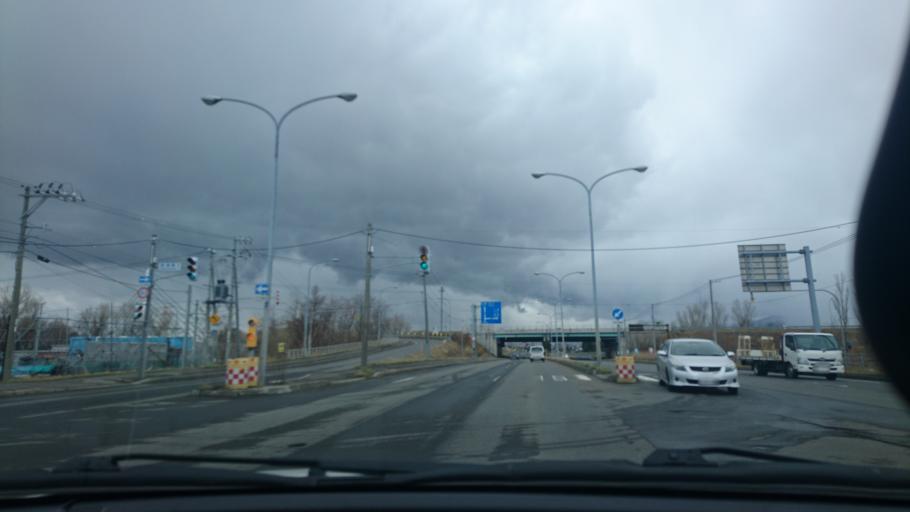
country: JP
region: Hokkaido
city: Ishikari
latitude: 43.1850
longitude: 141.3240
